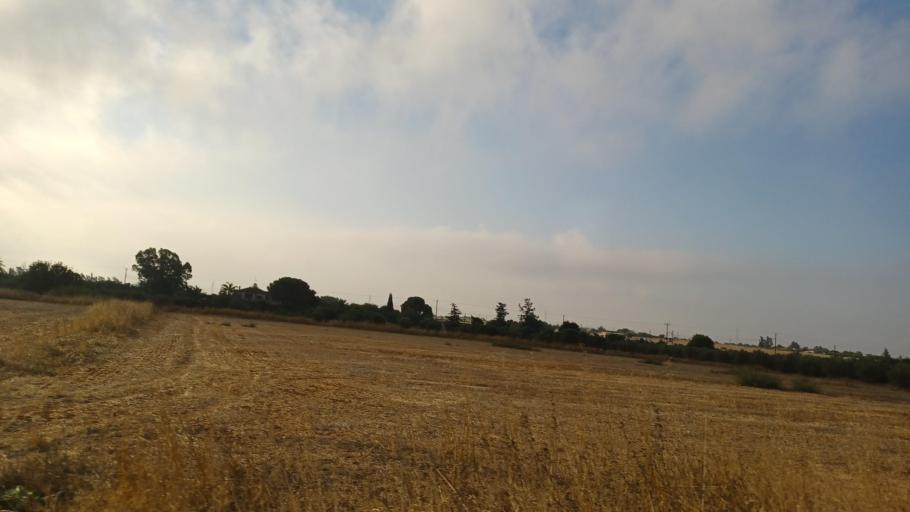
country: CY
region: Ammochostos
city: Avgorou
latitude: 35.0452
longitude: 33.8517
